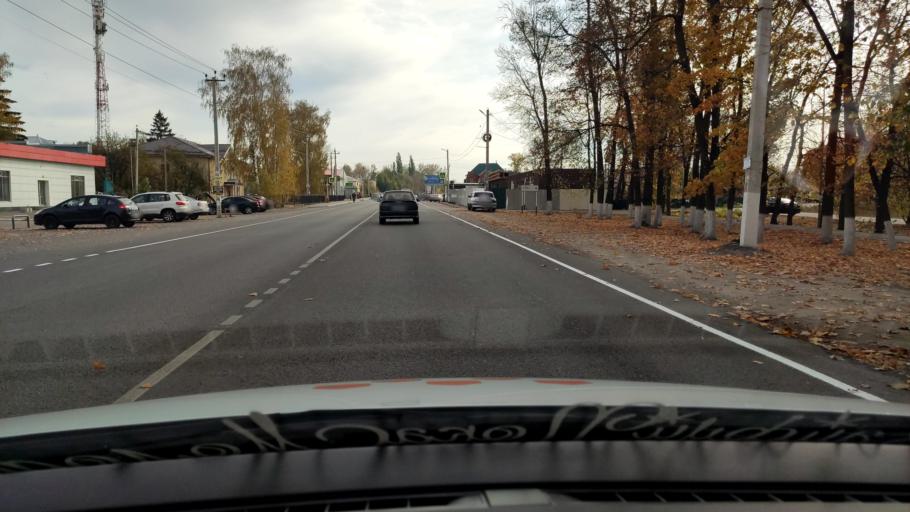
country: RU
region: Voronezj
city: Ramon'
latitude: 51.9105
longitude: 39.3301
